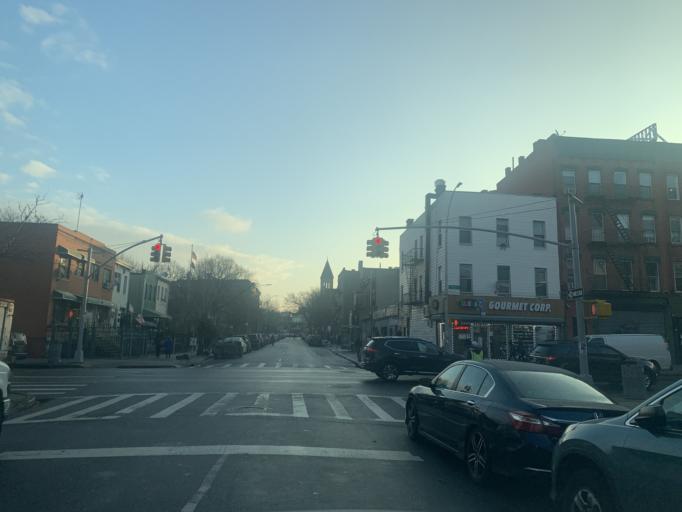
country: US
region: New York
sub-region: Kings County
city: Brooklyn
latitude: 40.6922
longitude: -73.9312
